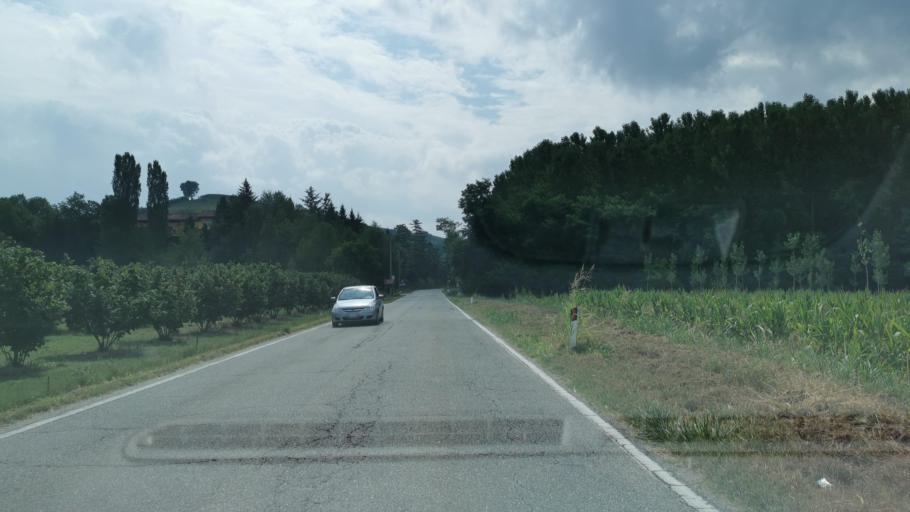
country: IT
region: Piedmont
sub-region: Provincia di Cuneo
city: Grinzane Cavour
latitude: 44.6502
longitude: 7.9927
